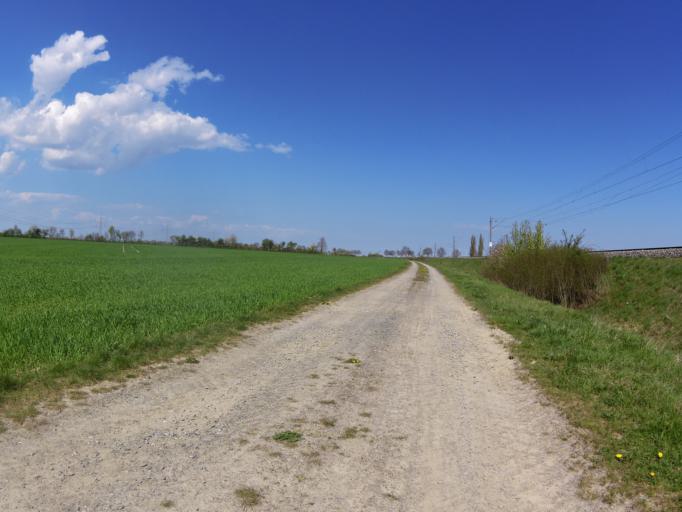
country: DE
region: Bavaria
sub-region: Regierungsbezirk Unterfranken
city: Oberpleichfeld
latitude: 49.8414
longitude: 10.1000
